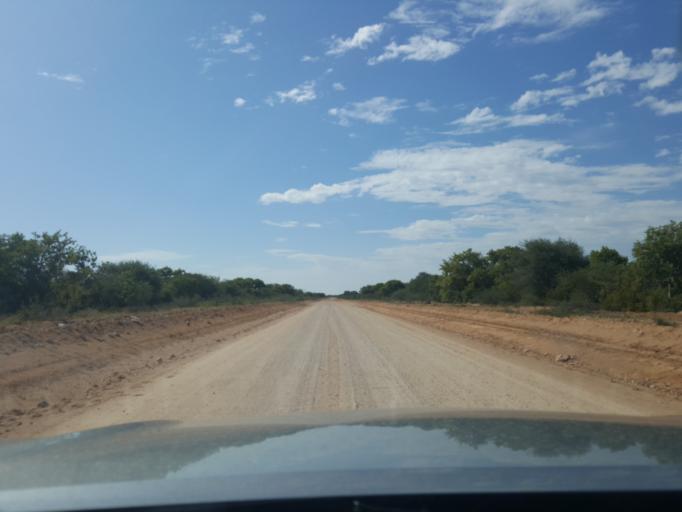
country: BW
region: Kweneng
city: Khudumelapye
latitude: -23.7521
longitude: 24.7557
